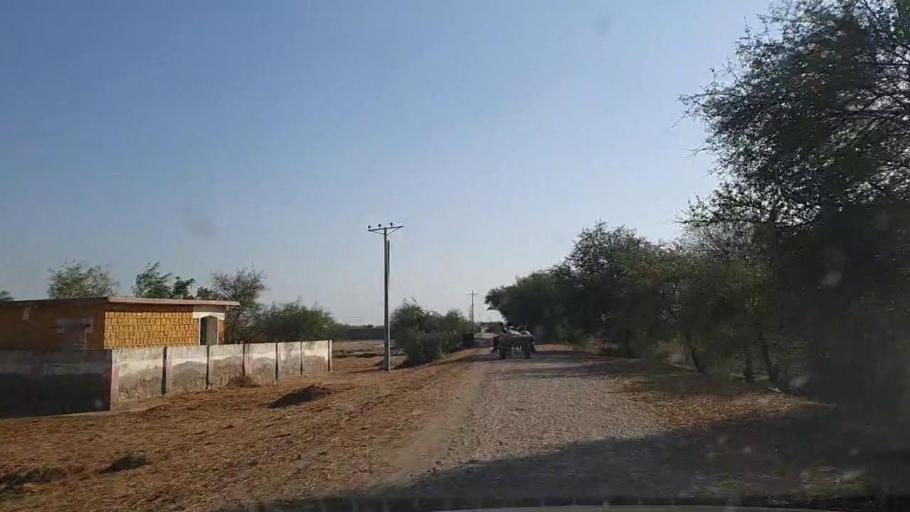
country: PK
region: Sindh
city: Thatta
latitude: 24.6217
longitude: 68.0779
